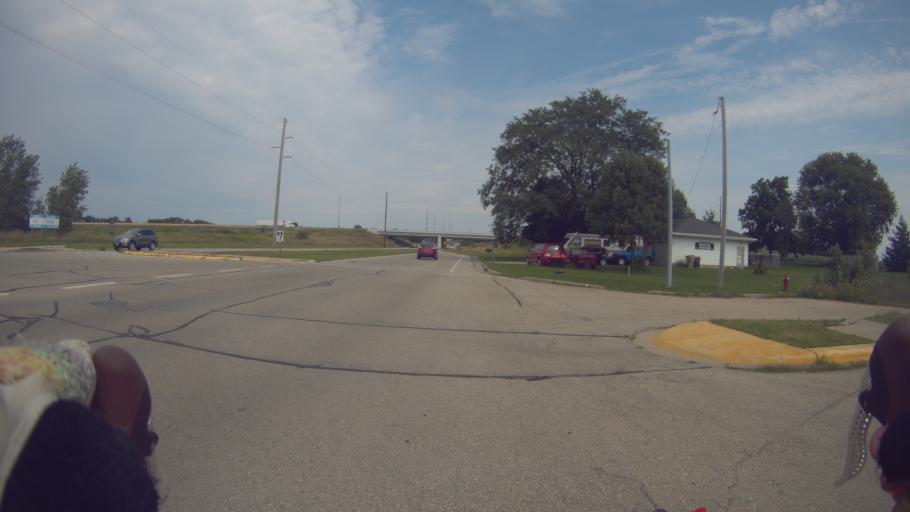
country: US
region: Wisconsin
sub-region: Dane County
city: Cottage Grove
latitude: 43.1015
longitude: -89.2666
